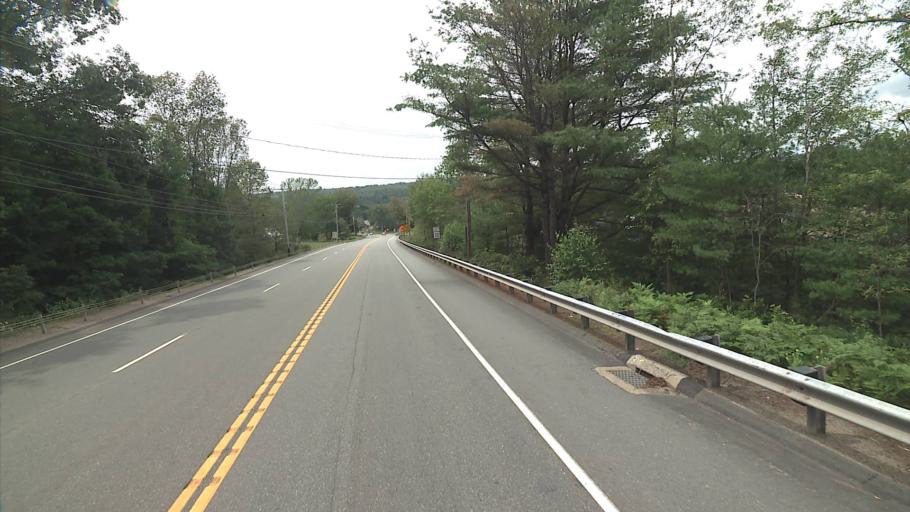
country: US
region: Connecticut
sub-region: Tolland County
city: Tolland
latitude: 41.8821
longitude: -72.2986
